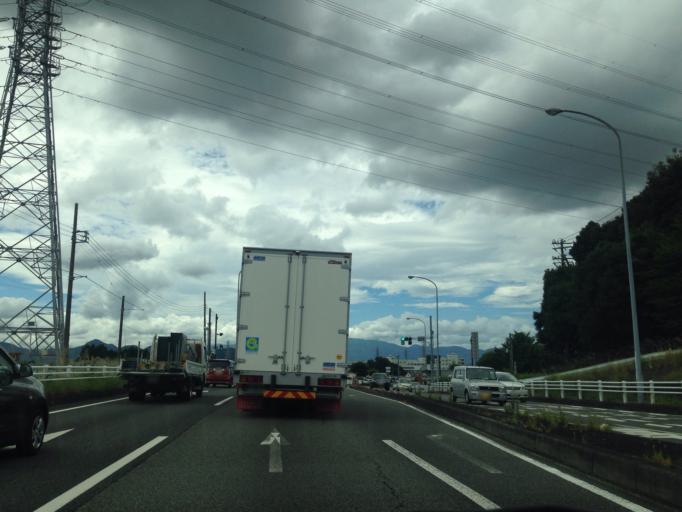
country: JP
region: Shizuoka
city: Mishima
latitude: 35.1414
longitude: 138.8861
